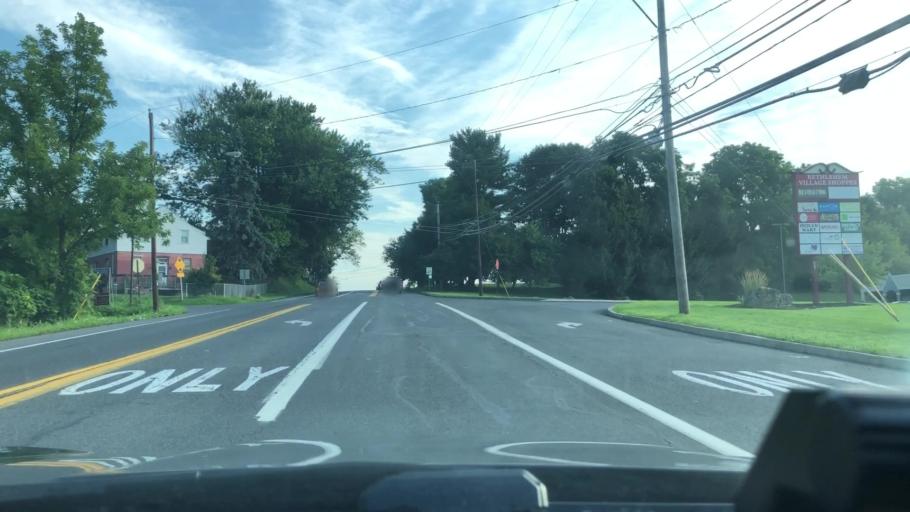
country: US
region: Pennsylvania
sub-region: Northampton County
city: Middletown
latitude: 40.6706
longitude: -75.3472
